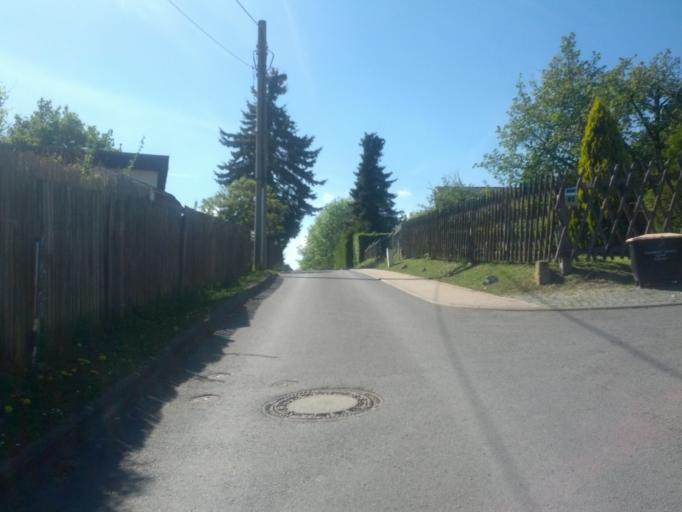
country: DE
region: Thuringia
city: Eisenach
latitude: 50.9866
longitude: 10.2927
